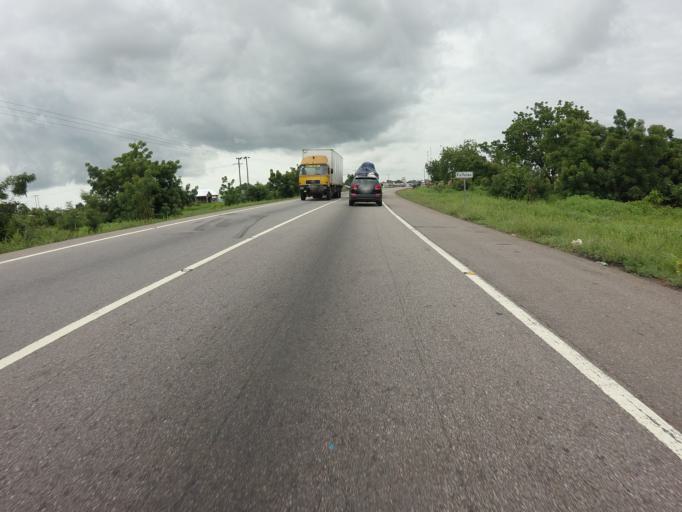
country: GH
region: Northern
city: Tamale
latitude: 9.1208
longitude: -1.2766
